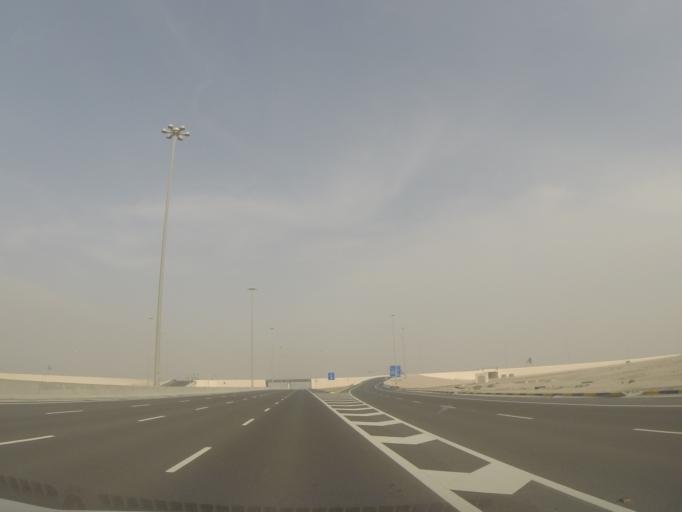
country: AE
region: Abu Dhabi
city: Abu Dhabi
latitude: 24.7727
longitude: 54.7156
